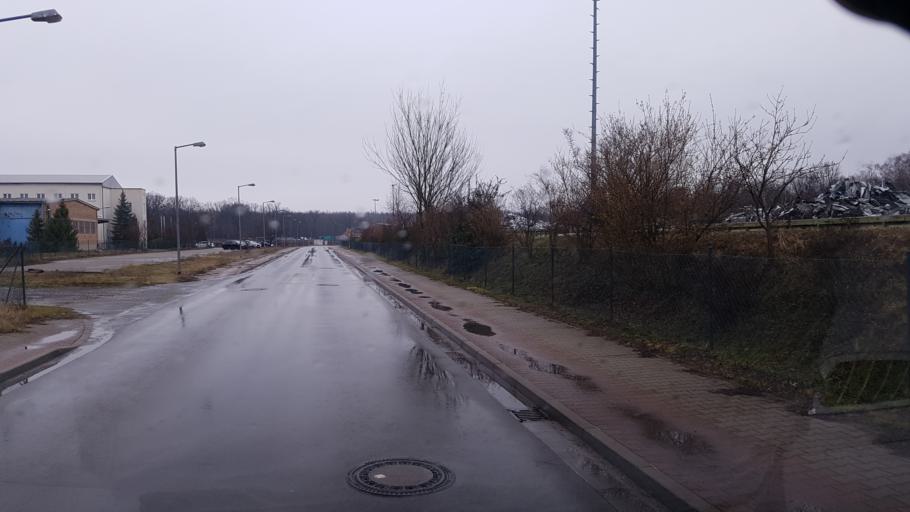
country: DE
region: Brandenburg
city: Lauchhammer
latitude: 51.5043
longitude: 13.8017
